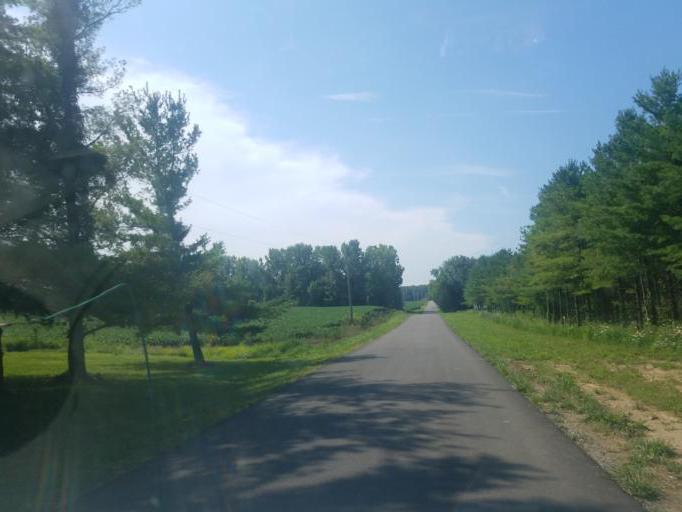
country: US
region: Ohio
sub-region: Knox County
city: Centerburg
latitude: 40.4236
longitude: -82.7189
